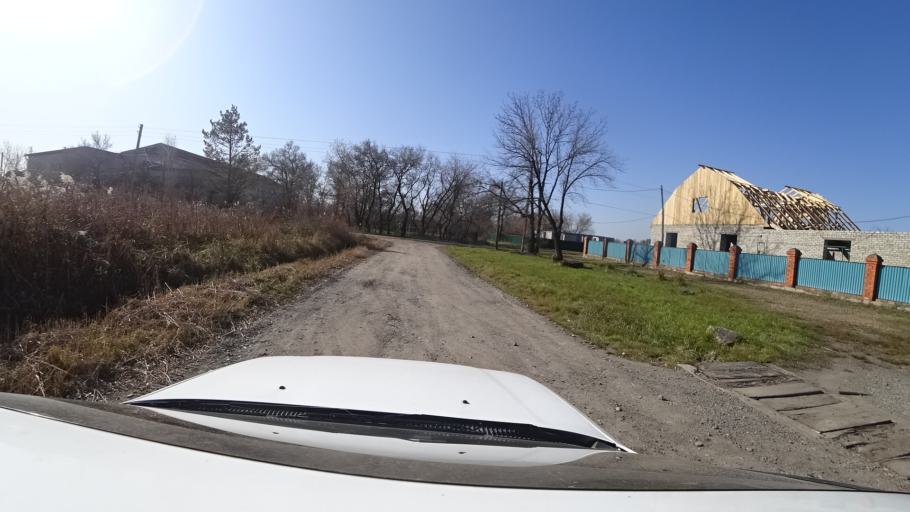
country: RU
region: Primorskiy
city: Lazo
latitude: 45.8780
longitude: 133.6439
